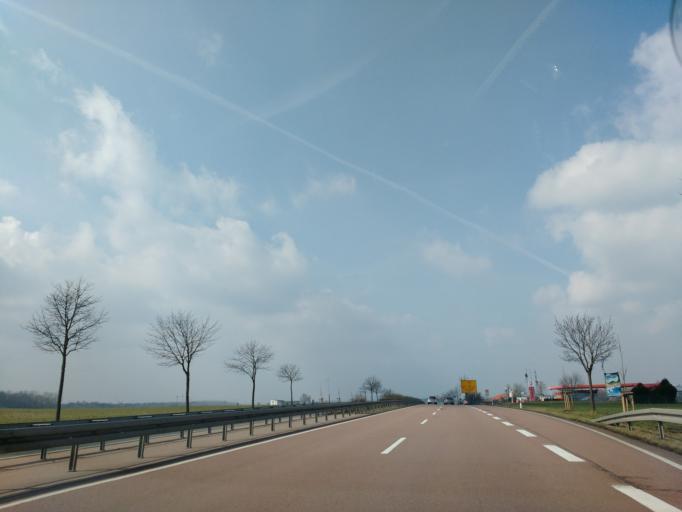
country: DE
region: Saxony-Anhalt
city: Langenbogen
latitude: 51.4794
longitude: 11.7871
